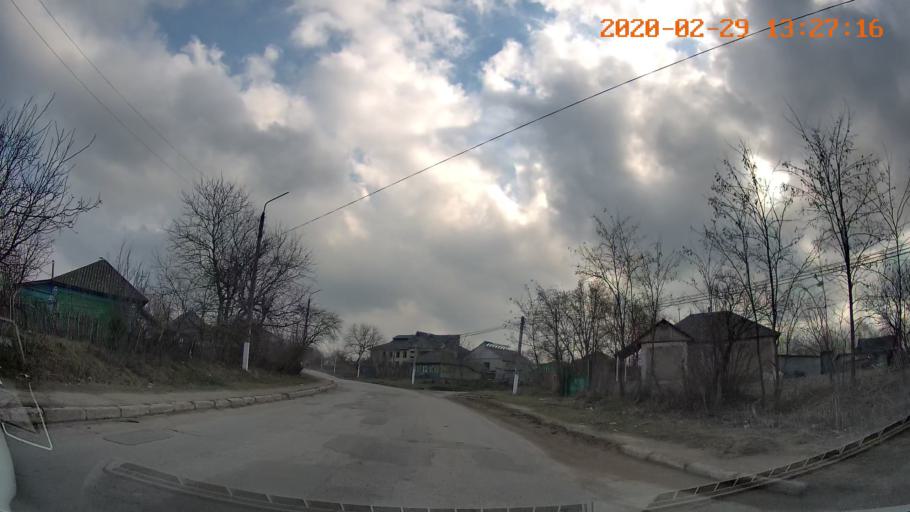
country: MD
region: Telenesti
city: Camenca
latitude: 47.9130
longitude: 28.6398
